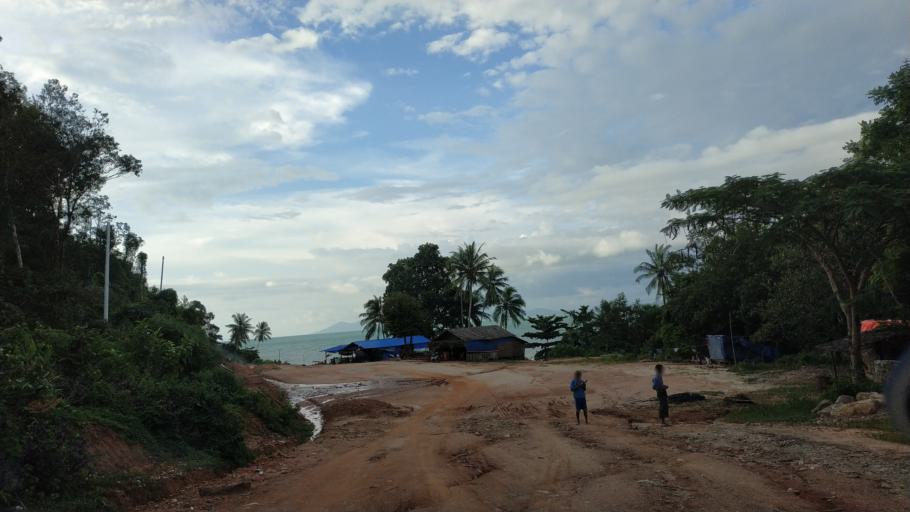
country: MM
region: Tanintharyi
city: Dawei
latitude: 14.0834
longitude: 98.0729
